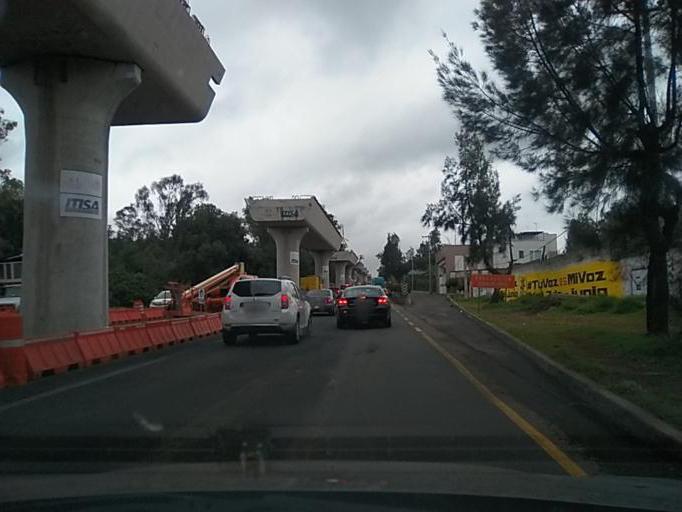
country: MX
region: Mexico City
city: Tlalpan
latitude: 19.2602
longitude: -99.1646
